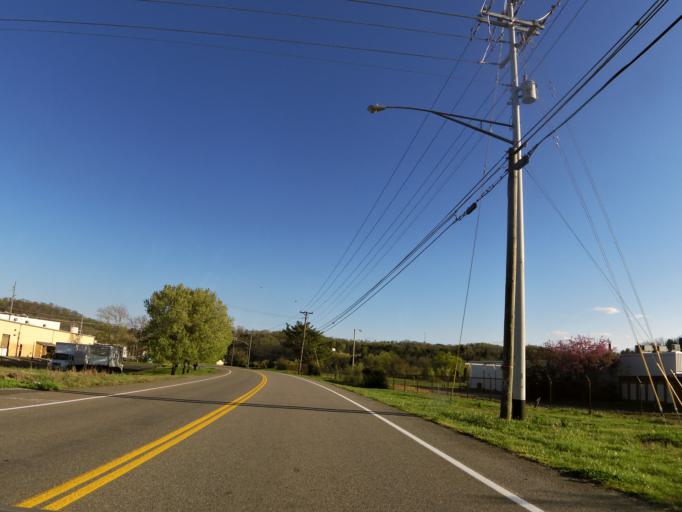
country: US
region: Tennessee
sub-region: Knox County
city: Knoxville
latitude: 35.9432
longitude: -83.8376
